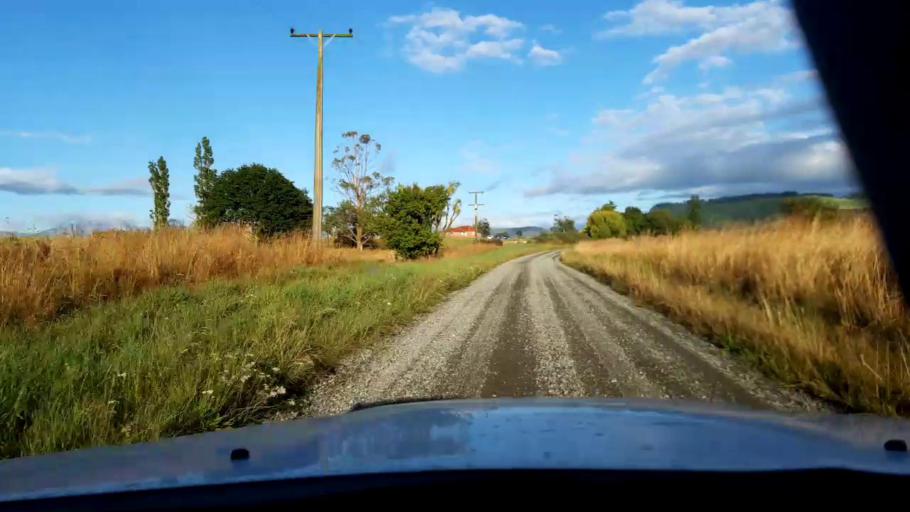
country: NZ
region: Canterbury
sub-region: Timaru District
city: Timaru
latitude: -44.4295
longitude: 171.1248
